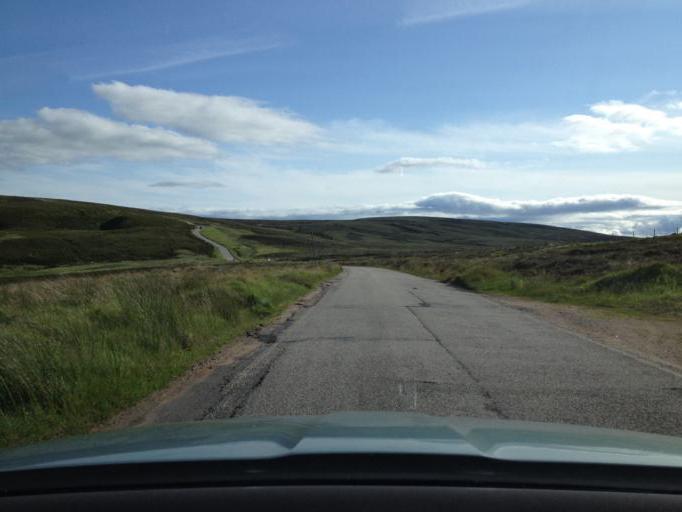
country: GB
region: Scotland
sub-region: Aberdeenshire
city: Laurencekirk
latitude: 56.9283
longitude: -2.5778
